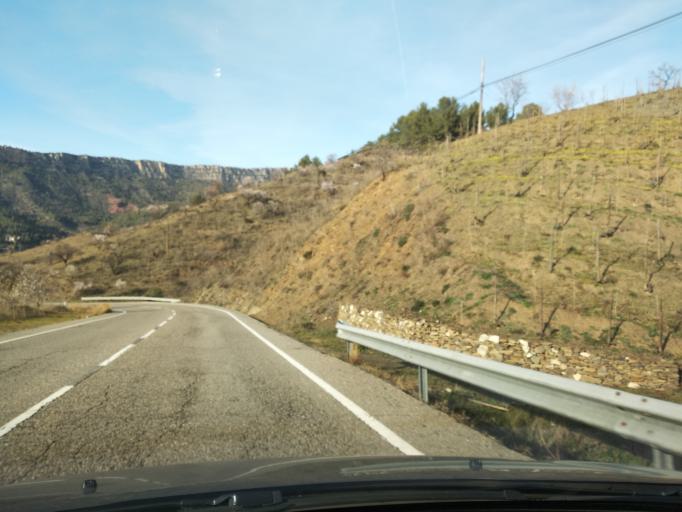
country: ES
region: Catalonia
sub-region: Provincia de Tarragona
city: Margalef
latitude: 41.2134
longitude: 0.7694
